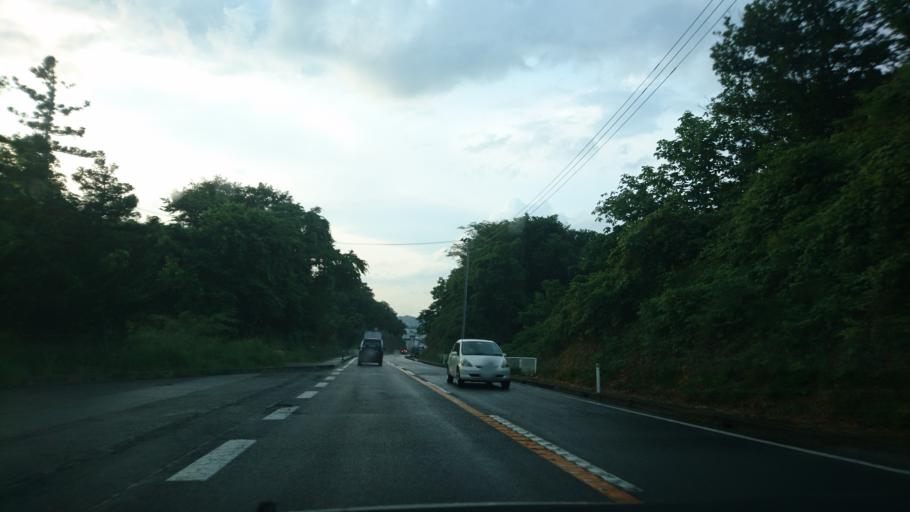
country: JP
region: Iwate
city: Ichinoseki
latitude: 38.9584
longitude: 141.1224
